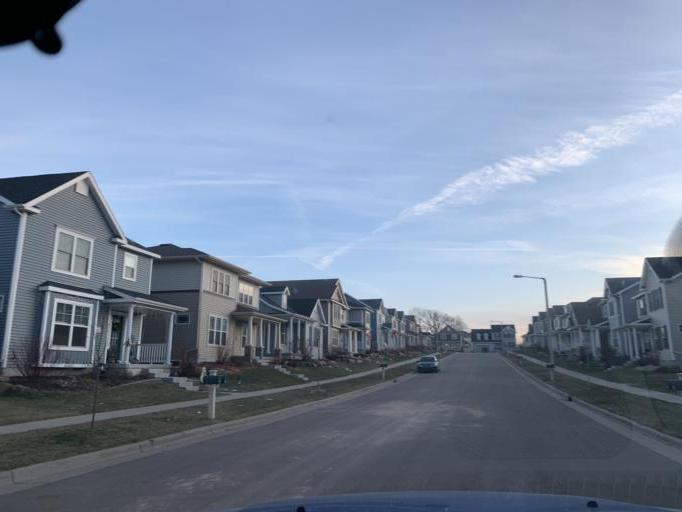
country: US
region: Wisconsin
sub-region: Dane County
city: Middleton
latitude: 43.0588
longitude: -89.5652
